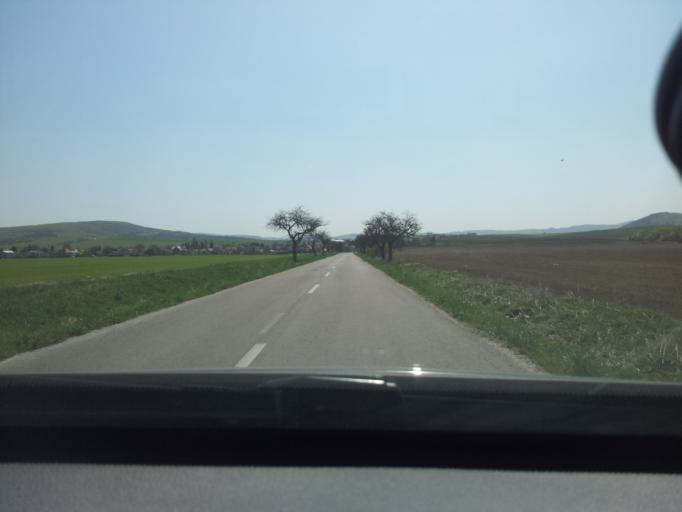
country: SK
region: Nitriansky
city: Partizanske
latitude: 48.5974
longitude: 18.2839
